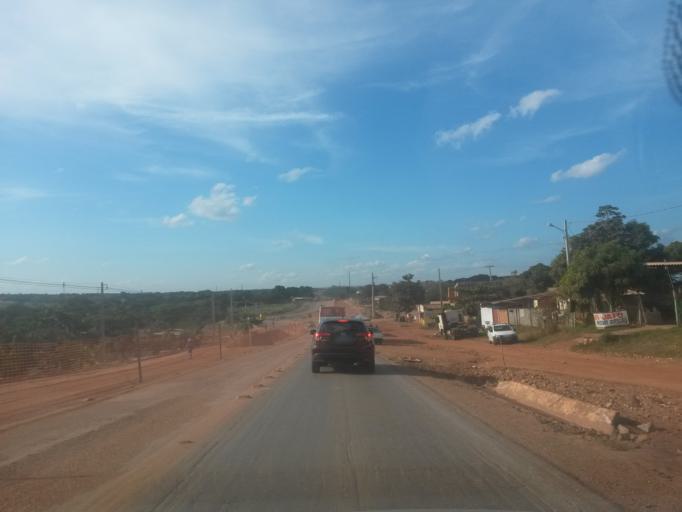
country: BR
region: Mato Grosso
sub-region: Cuiaba
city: Cuiaba
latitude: -15.5408
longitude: -56.0787
